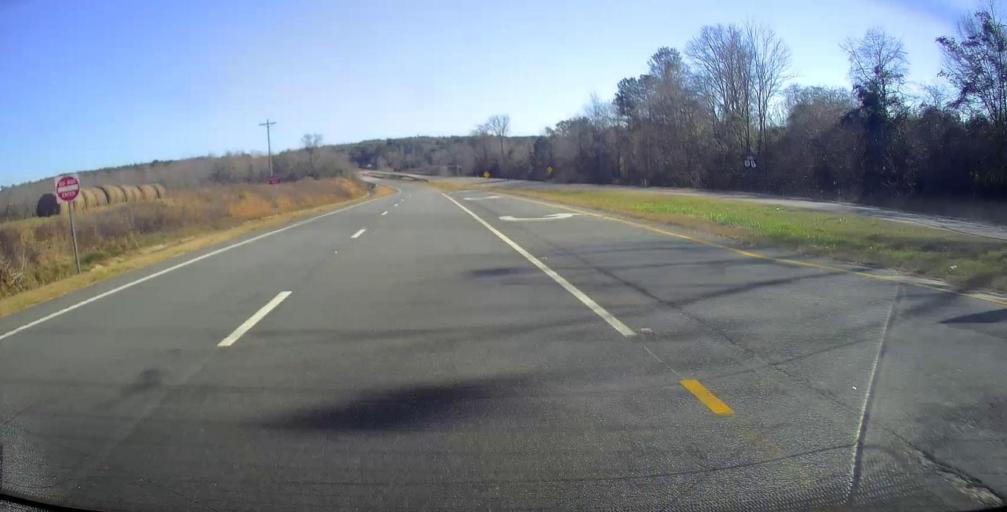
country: US
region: Georgia
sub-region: Taylor County
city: Butler
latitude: 32.6224
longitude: -84.2481
